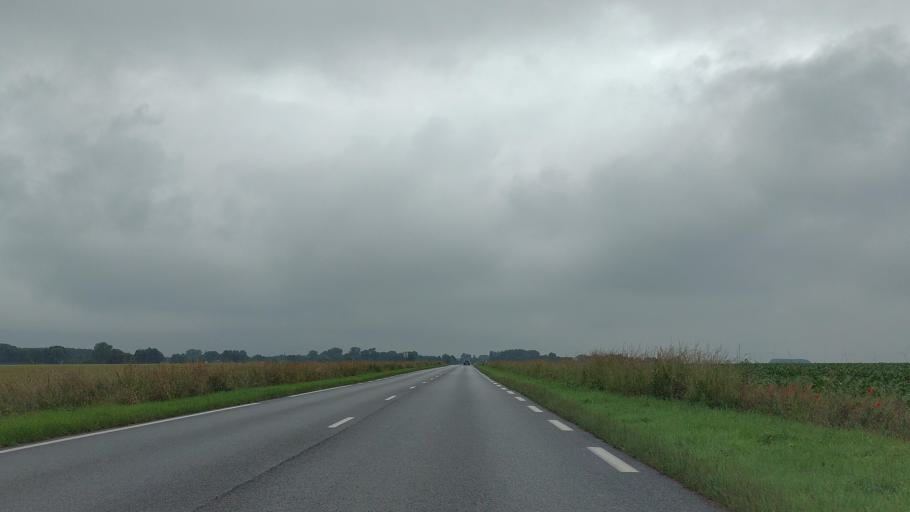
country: FR
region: Picardie
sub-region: Departement de la Somme
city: Chepy
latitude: 50.0842
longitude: 1.6525
